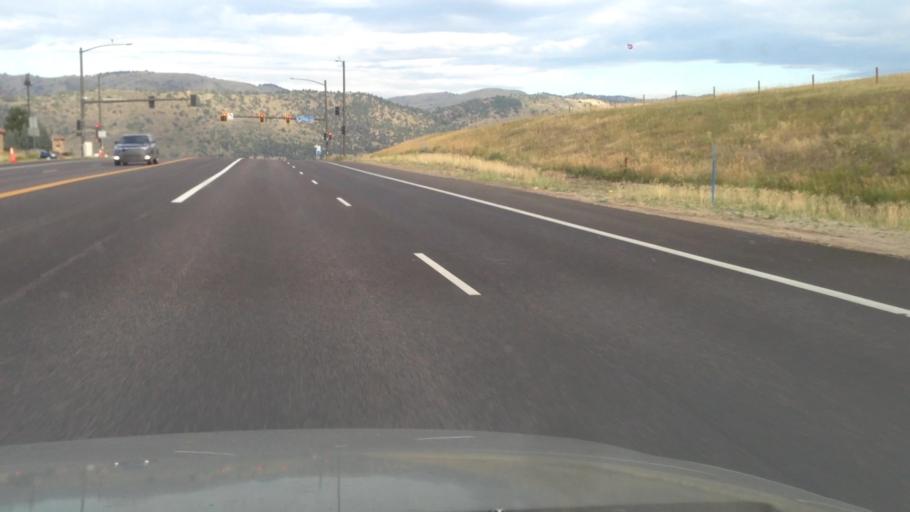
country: US
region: Colorado
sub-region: Jefferson County
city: West Pleasant View
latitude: 39.6813
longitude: -105.1713
